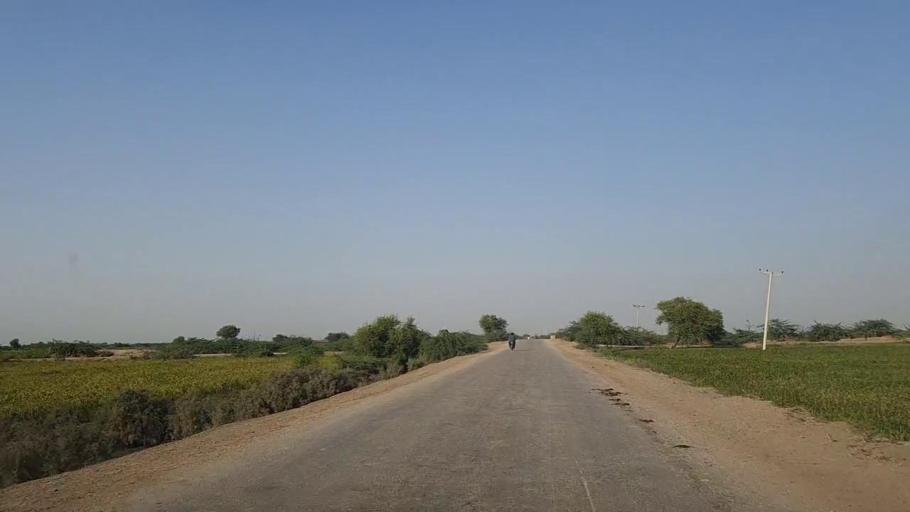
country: PK
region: Sindh
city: Mirpur Batoro
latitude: 24.5981
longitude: 68.4001
